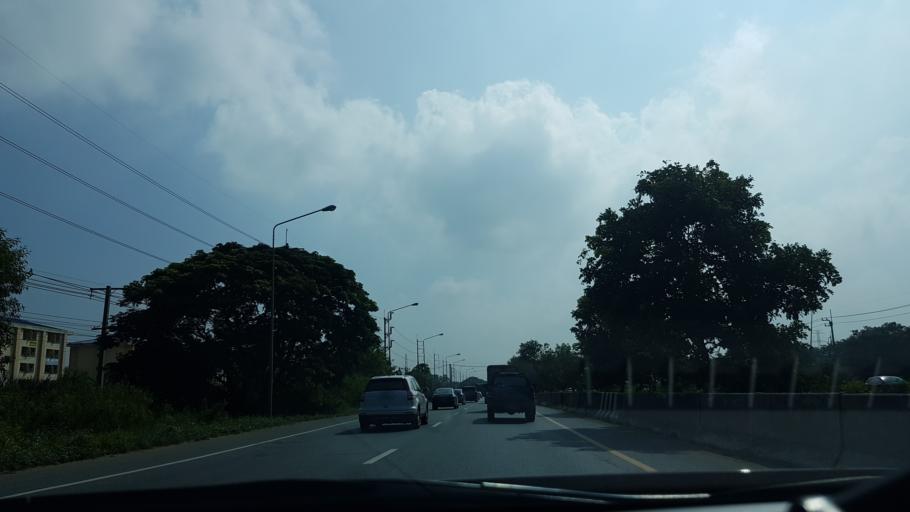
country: TH
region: Phra Nakhon Si Ayutthaya
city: Bang Pa-in
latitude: 14.1695
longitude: 100.6018
